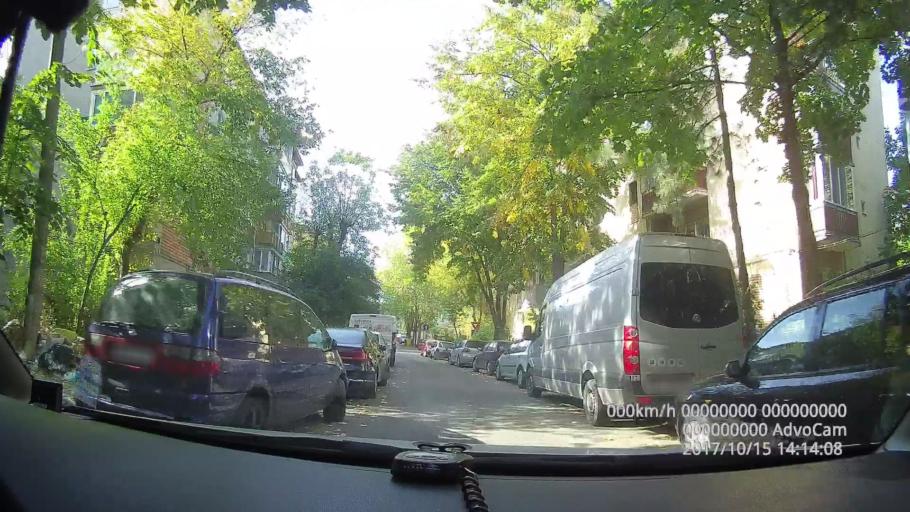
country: RO
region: Timis
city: Timisoara
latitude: 45.7732
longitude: 21.2180
